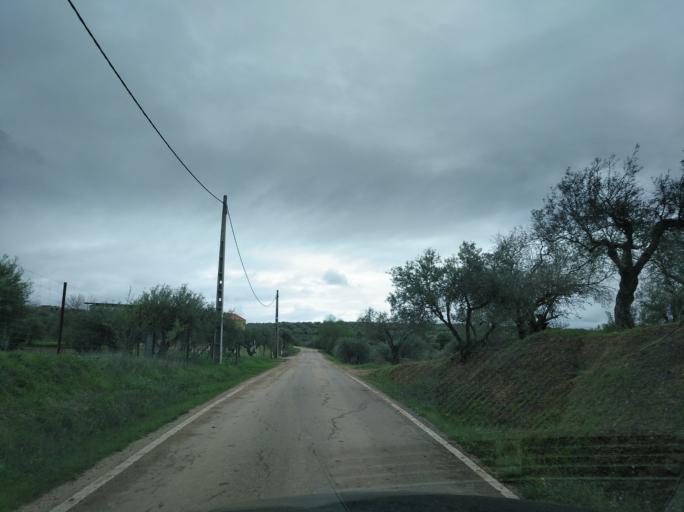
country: PT
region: Portalegre
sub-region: Campo Maior
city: Campo Maior
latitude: 38.9893
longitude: -7.0459
